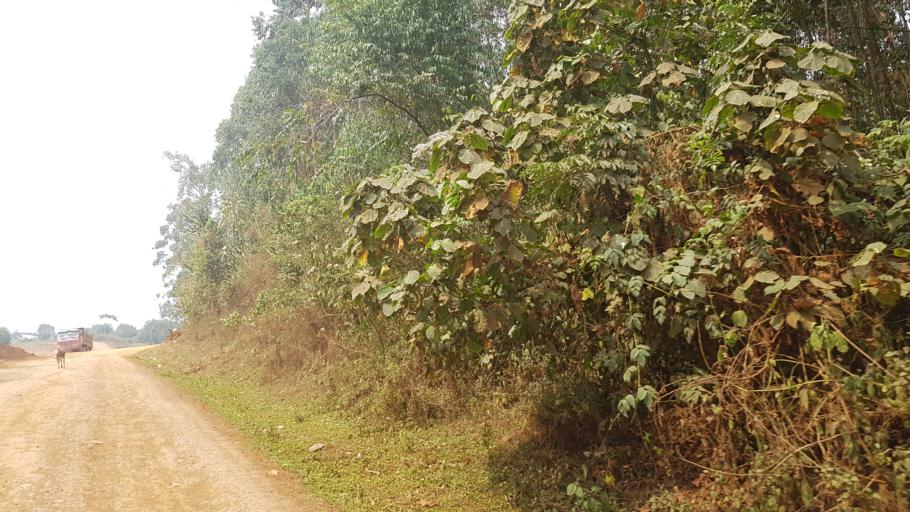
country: ET
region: Oromiya
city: Gore
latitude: 7.8178
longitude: 35.4598
